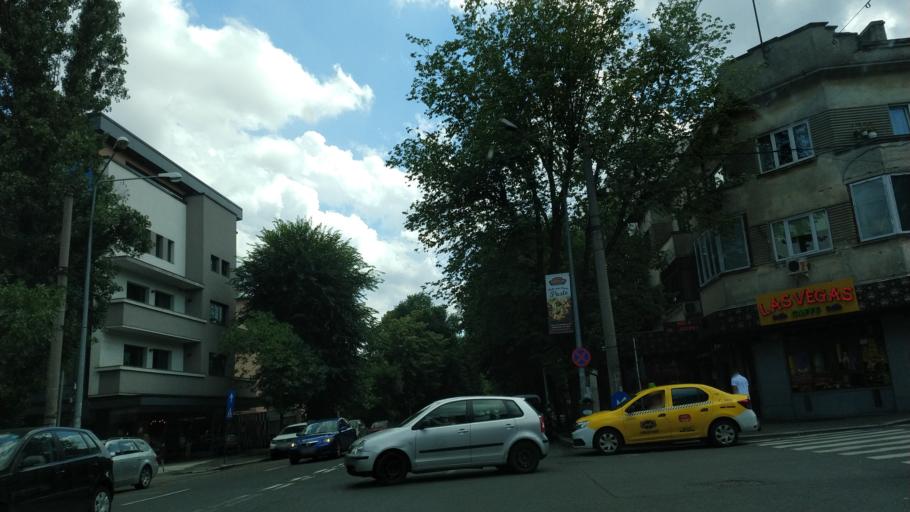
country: RO
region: Bucuresti
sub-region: Municipiul Bucuresti
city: Bucharest
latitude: 44.4622
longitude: 26.1013
